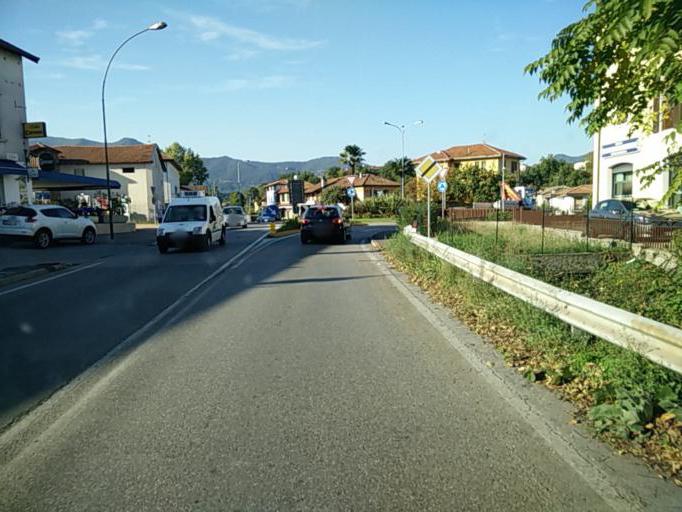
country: IT
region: Lombardy
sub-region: Provincia di Brescia
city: Cunettone-Villa
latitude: 45.5864
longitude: 10.5177
